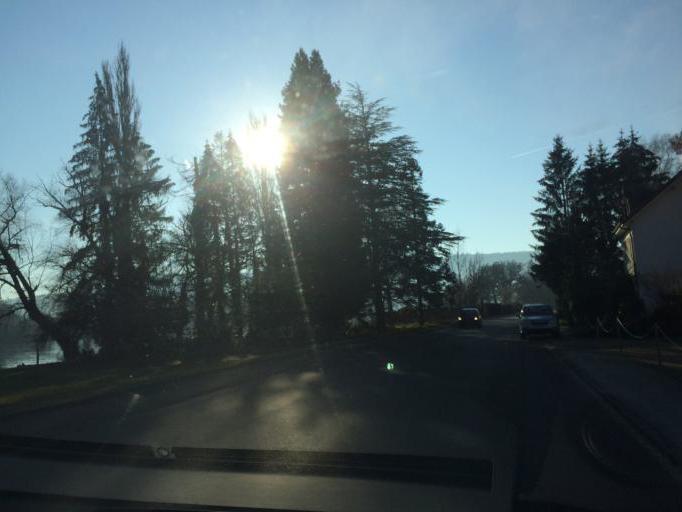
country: DE
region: Baden-Wuerttemberg
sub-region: Freiburg Region
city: Busingen
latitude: 47.6925
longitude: 8.6844
